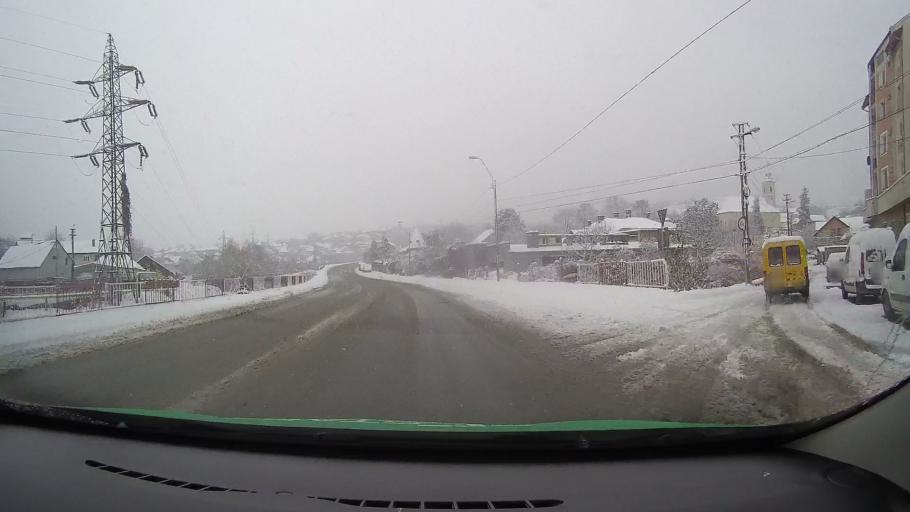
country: RO
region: Hunedoara
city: Hunedoara
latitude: 45.7493
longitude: 22.8930
